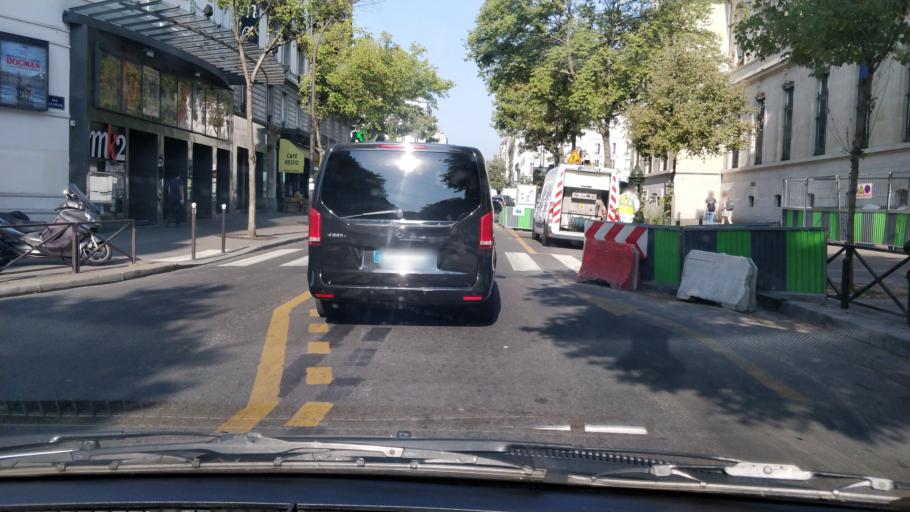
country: FR
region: Ile-de-France
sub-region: Departement de Seine-Saint-Denis
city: Bagnolet
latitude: 48.8648
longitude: 2.3999
